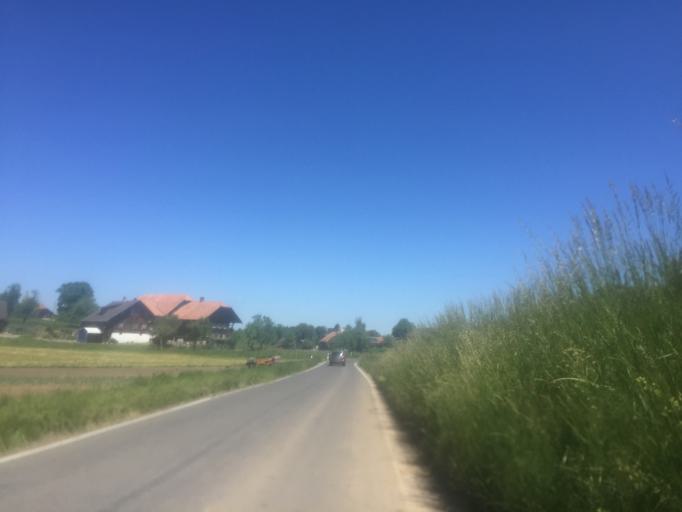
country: CH
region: Bern
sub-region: Thun District
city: Thierachern
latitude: 46.7471
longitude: 7.5645
